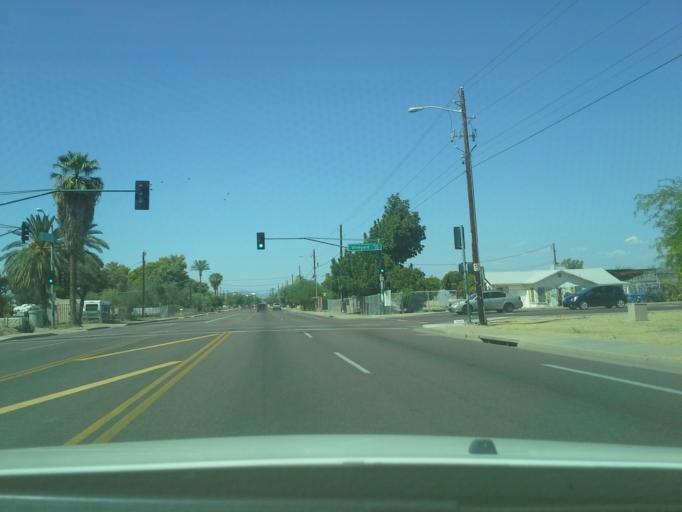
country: US
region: Arizona
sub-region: Maricopa County
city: Phoenix
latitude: 33.3846
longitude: -112.0646
